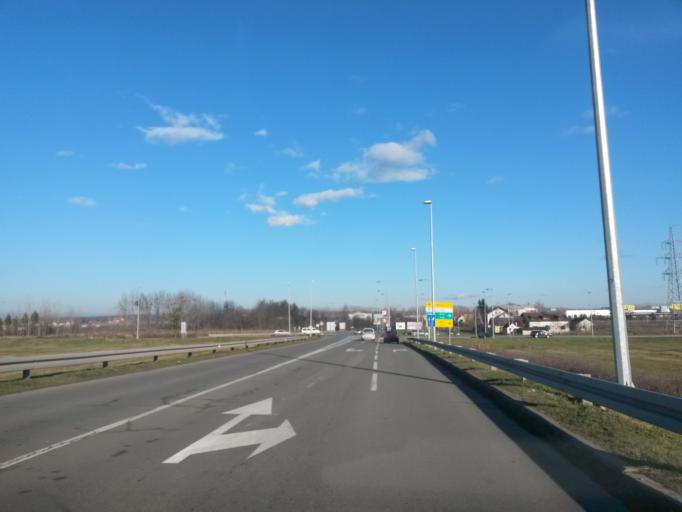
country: HR
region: Osjecko-Baranjska
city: Visnjevac
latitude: 45.5548
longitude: 18.6344
